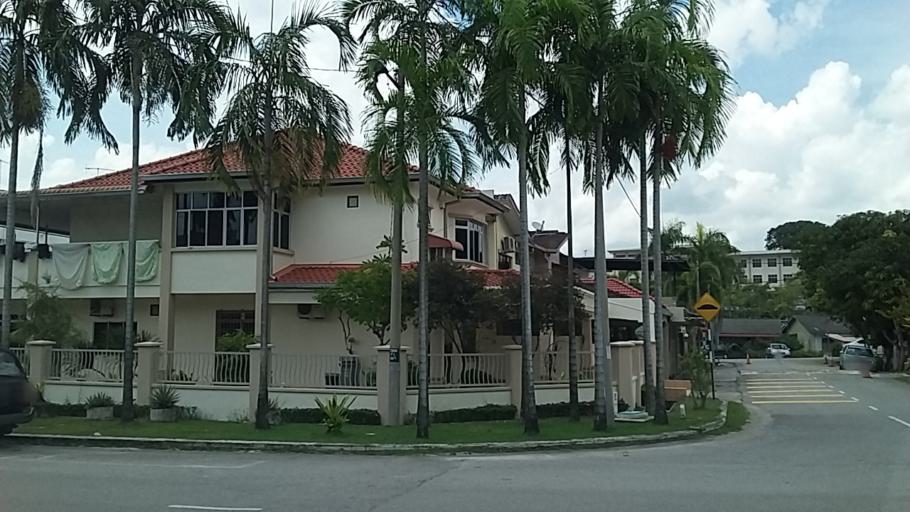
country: MY
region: Johor
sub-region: Daerah Batu Pahat
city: Batu Pahat
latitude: 1.8363
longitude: 102.9466
